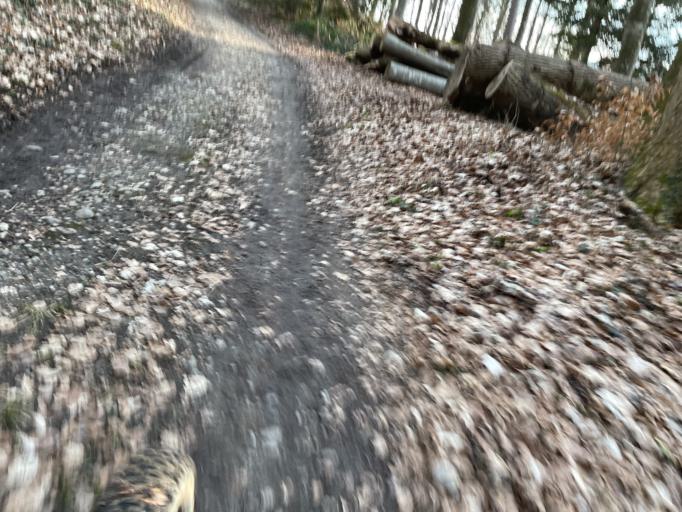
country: CH
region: Bern
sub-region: Bern-Mittelland District
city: Toffen
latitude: 46.8495
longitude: 7.5111
